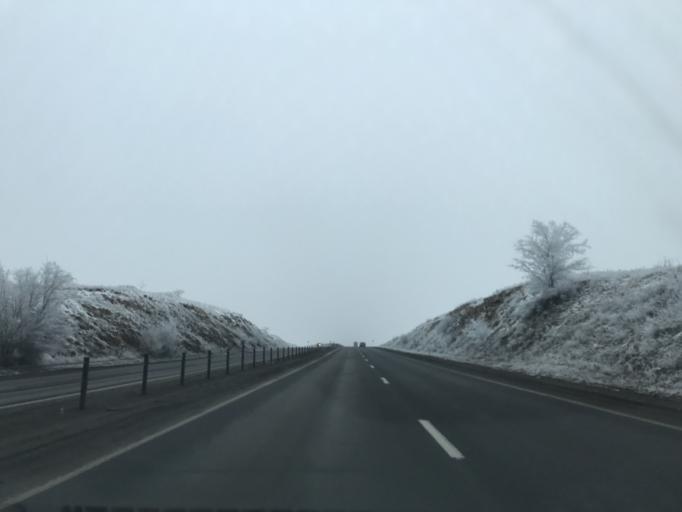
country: RU
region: Rostov
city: Likhoy
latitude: 48.1460
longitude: 40.2603
